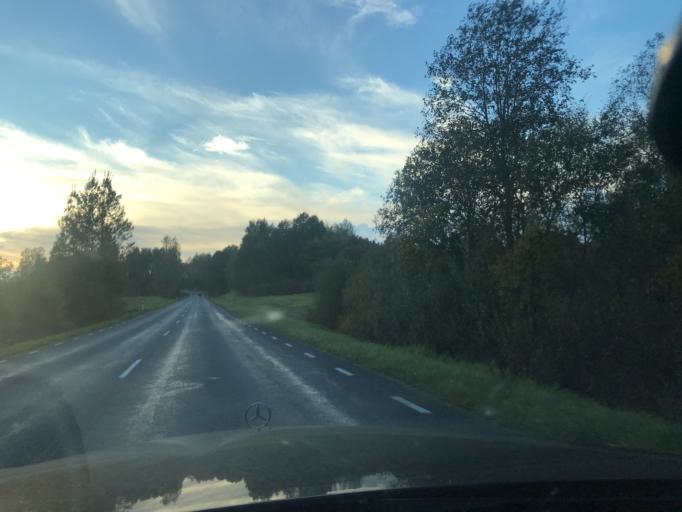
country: EE
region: Vorumaa
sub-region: Antsla vald
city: Vana-Antsla
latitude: 57.8776
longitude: 26.6494
